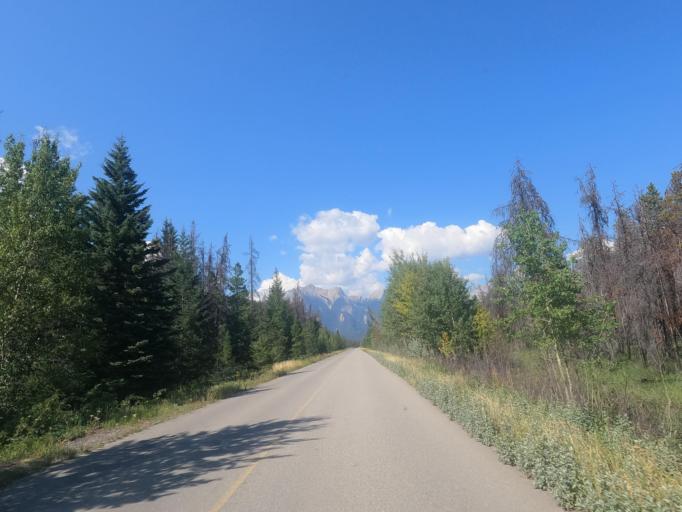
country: CA
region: Alberta
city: Jasper Park Lodge
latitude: 52.9823
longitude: -118.0738
